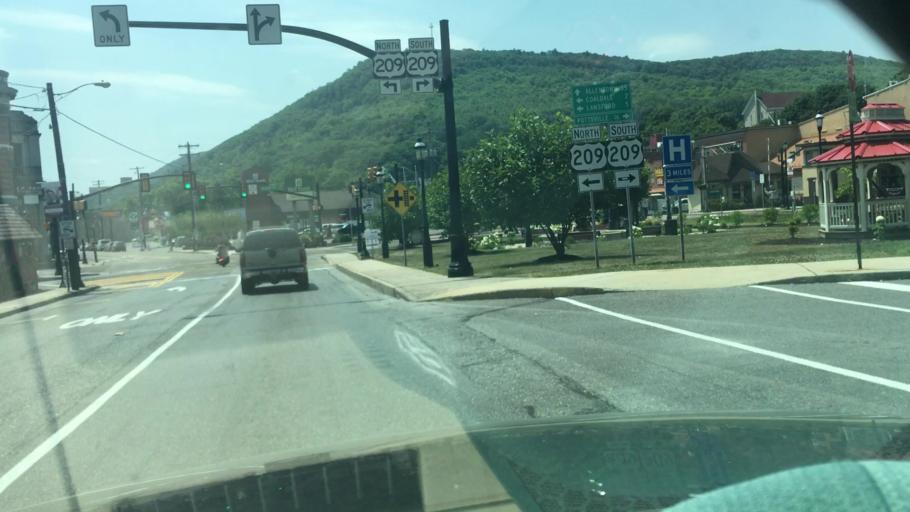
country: US
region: Pennsylvania
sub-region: Schuylkill County
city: Tamaqua
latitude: 40.7979
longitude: -75.9695
